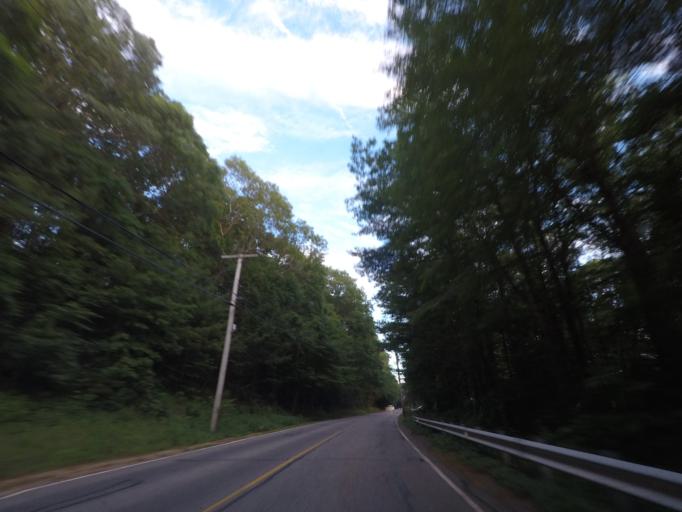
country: US
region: Massachusetts
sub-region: Worcester County
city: Warren
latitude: 42.1959
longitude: -72.1806
